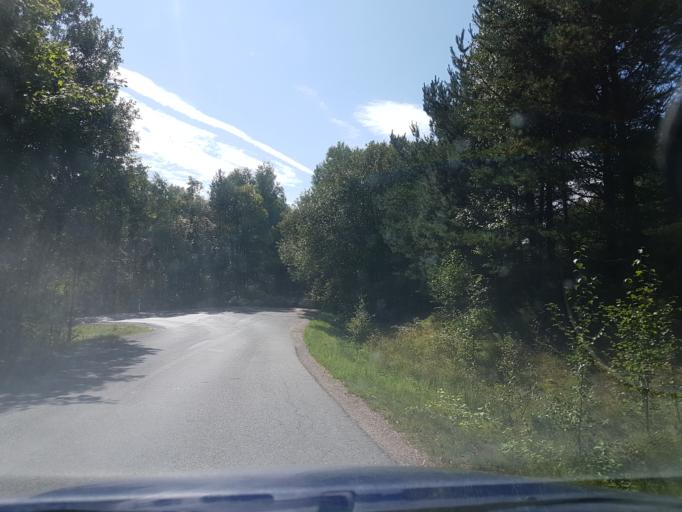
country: SE
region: Vaestra Goetaland
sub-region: Lerums Kommun
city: Grabo
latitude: 57.8503
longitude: 12.3086
